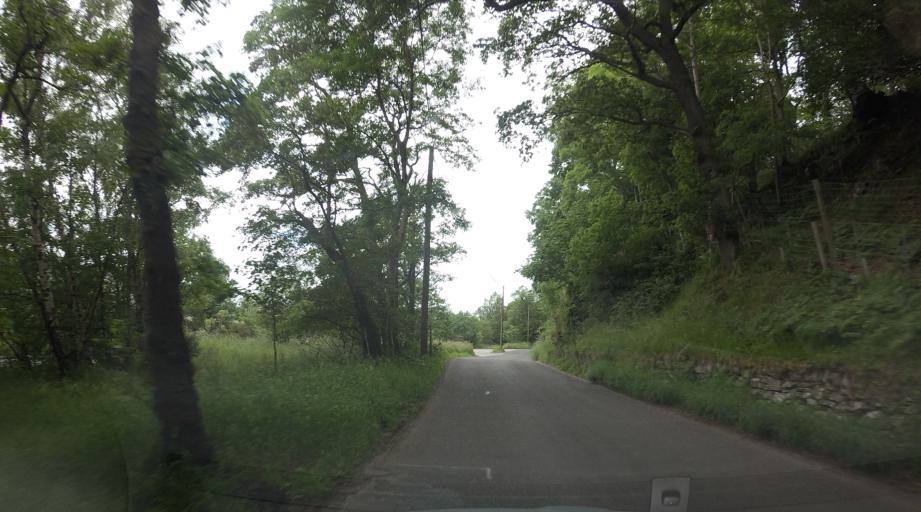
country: GB
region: Scotland
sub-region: Perth and Kinross
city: Aberfeldy
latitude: 56.7018
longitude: -4.1740
